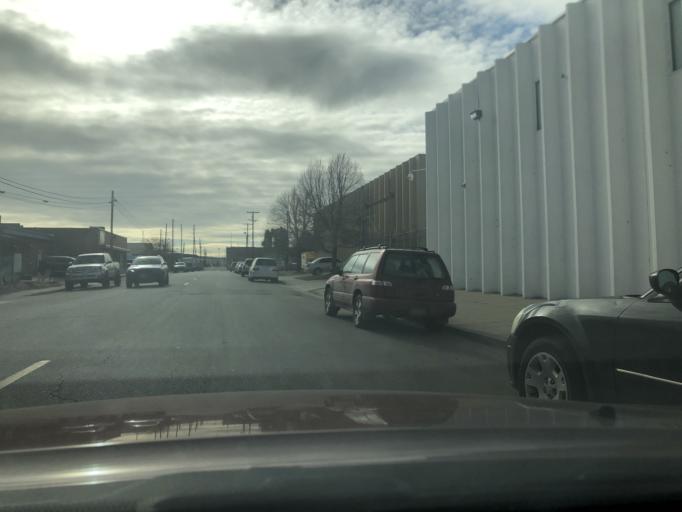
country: US
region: Colorado
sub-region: Arapahoe County
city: Englewood
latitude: 39.6911
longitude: -104.9911
